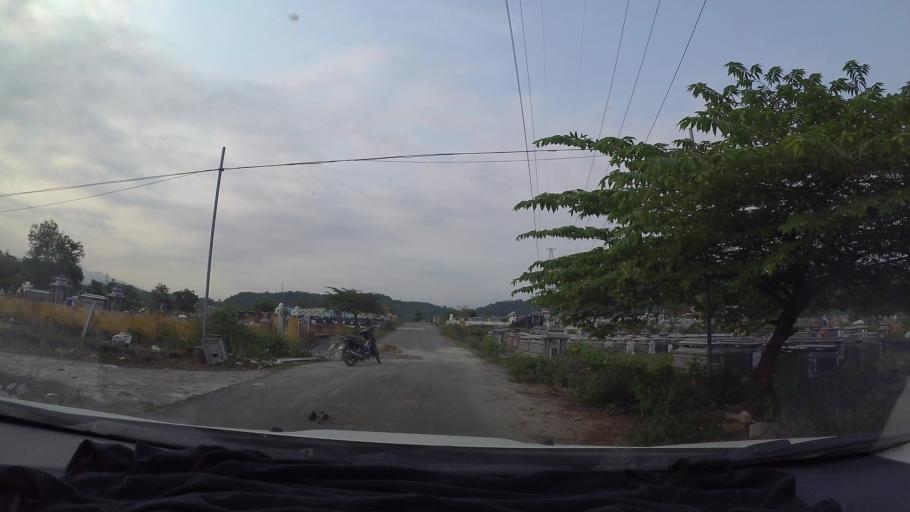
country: VN
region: Da Nang
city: Lien Chieu
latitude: 16.0563
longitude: 108.1090
